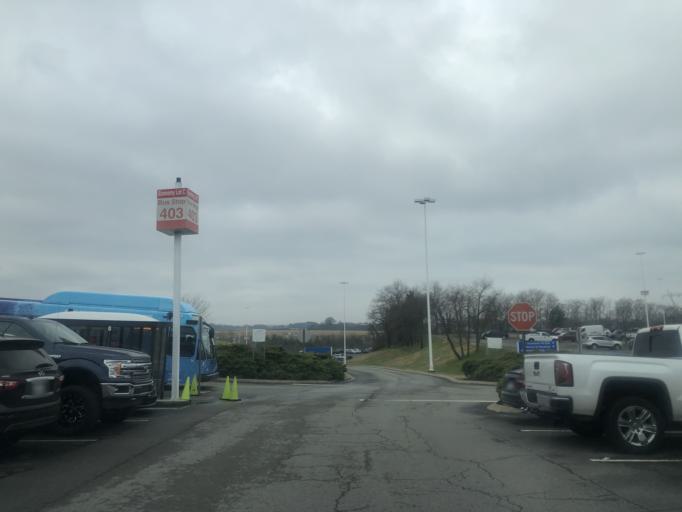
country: US
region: Tennessee
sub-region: Davidson County
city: Lakewood
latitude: 36.1385
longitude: -86.6682
